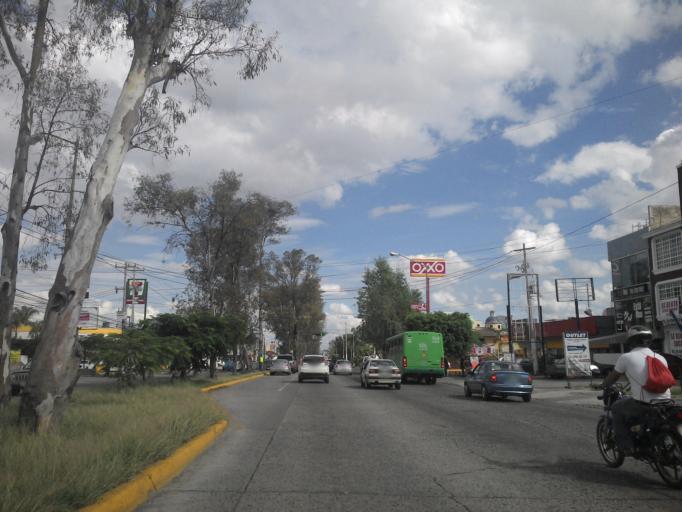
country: MX
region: Jalisco
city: Guadalajara
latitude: 20.6590
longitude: -103.4433
